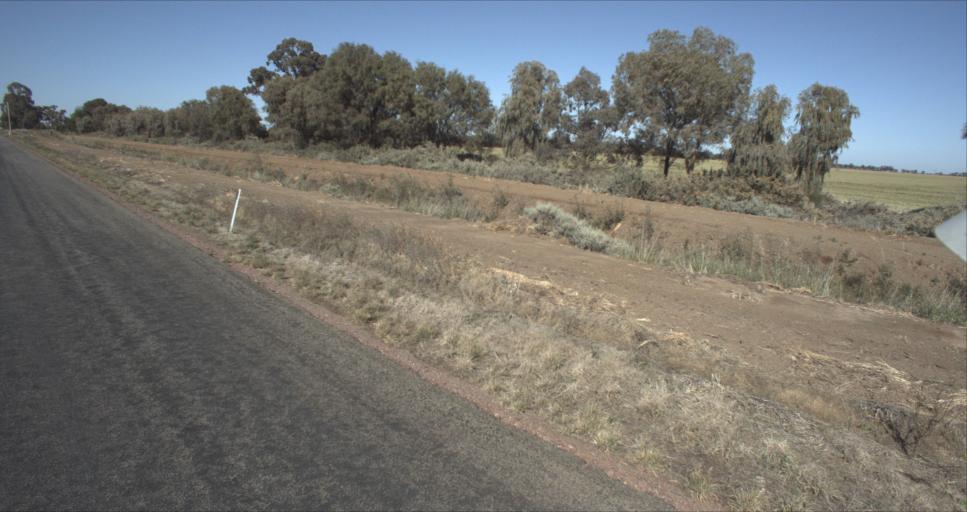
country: AU
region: New South Wales
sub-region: Leeton
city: Leeton
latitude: -34.5519
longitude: 146.2672
